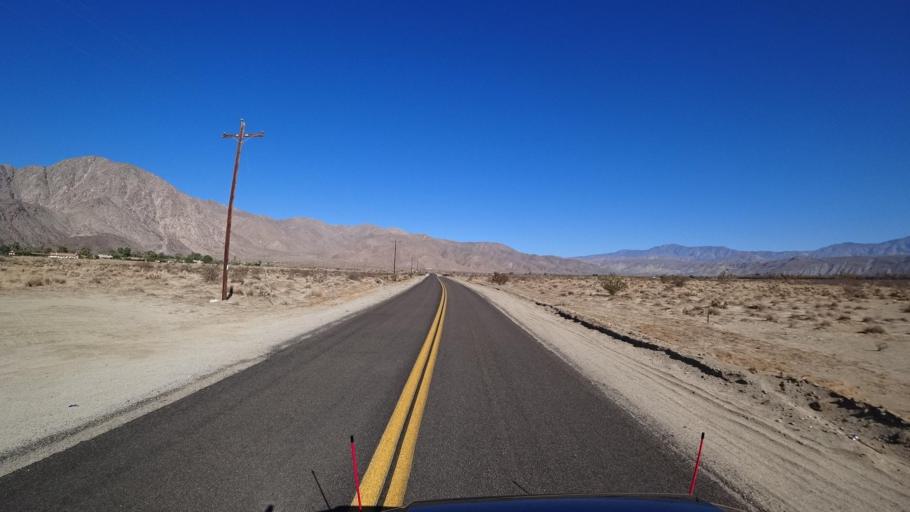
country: US
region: California
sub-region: San Diego County
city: Borrego Springs
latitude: 33.2943
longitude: -116.3795
